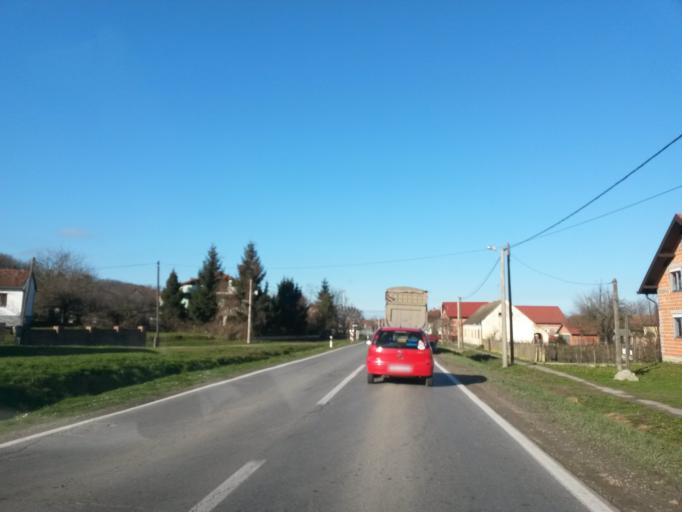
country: HR
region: Virovitick-Podravska
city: Suhopolje
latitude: 45.7508
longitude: 17.5851
